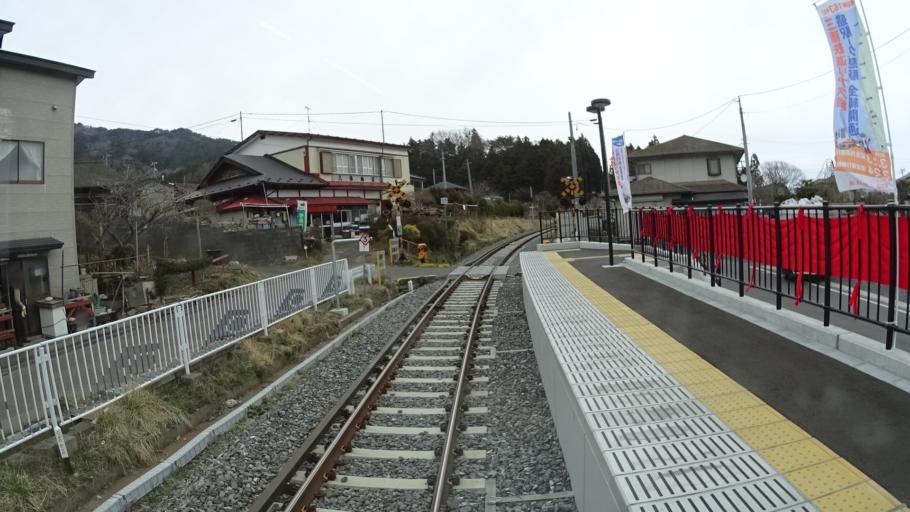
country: JP
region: Iwate
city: Otsuchi
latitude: 39.3839
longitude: 141.9352
